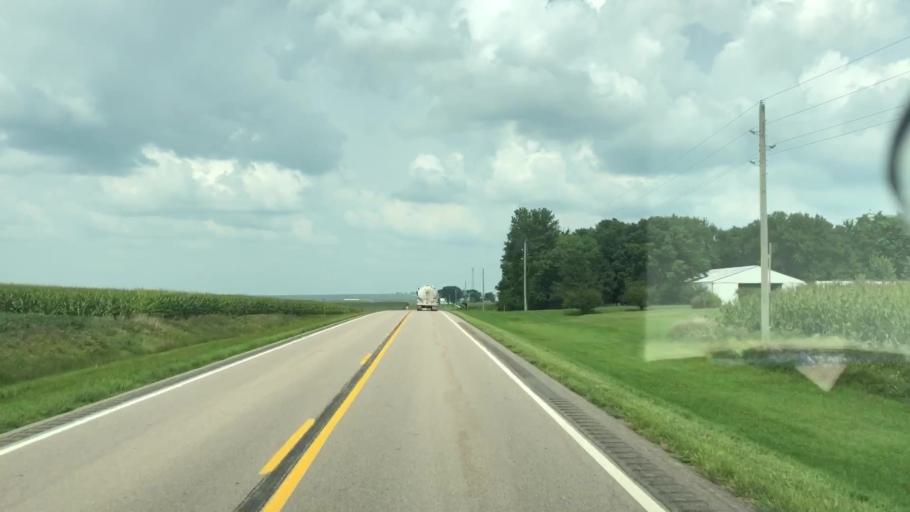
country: US
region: Iowa
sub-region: Plymouth County
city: Remsen
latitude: 42.7967
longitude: -95.9577
